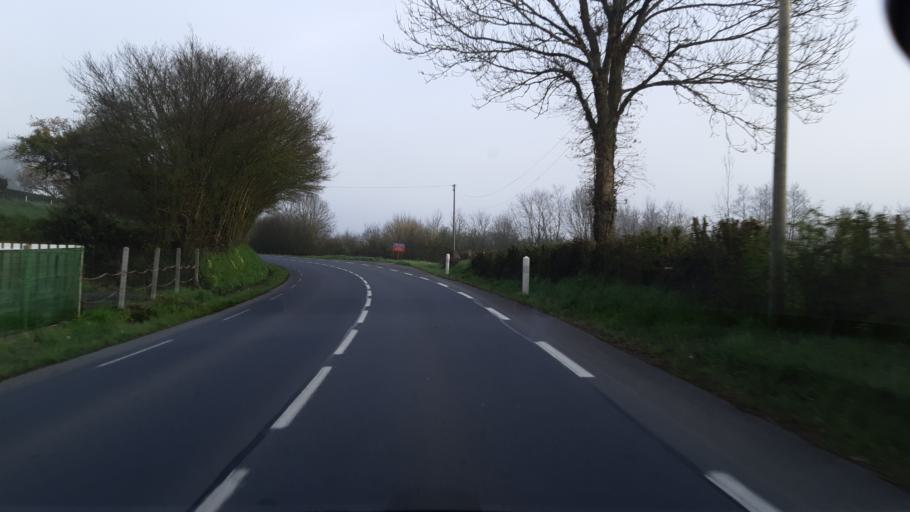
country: FR
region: Lower Normandy
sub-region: Departement de la Manche
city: Agneaux
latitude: 49.0874
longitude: -1.1146
